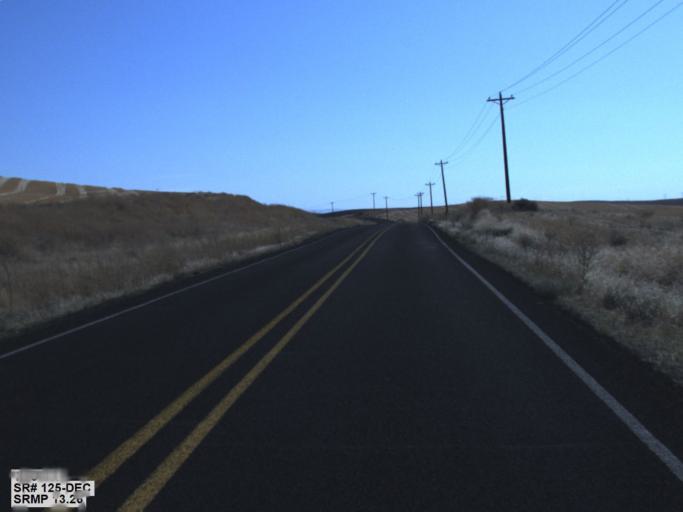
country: US
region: Washington
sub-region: Walla Walla County
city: Walla Walla
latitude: 46.1613
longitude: -118.3793
